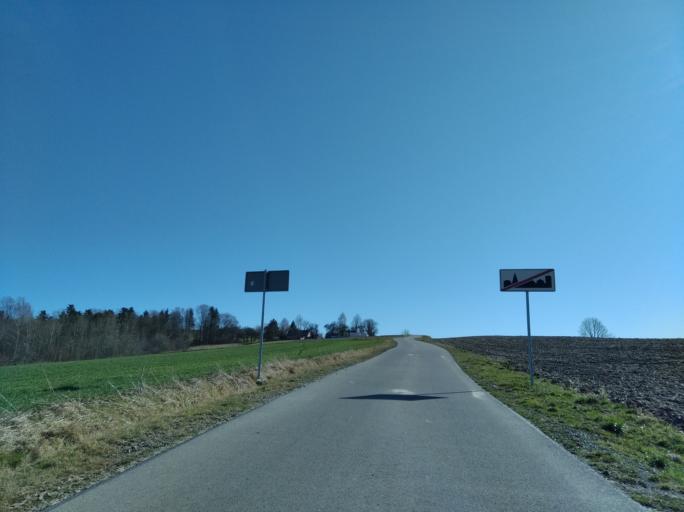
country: PL
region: Subcarpathian Voivodeship
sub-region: Powiat strzyzowski
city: Wisniowa
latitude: 49.9102
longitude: 21.6976
